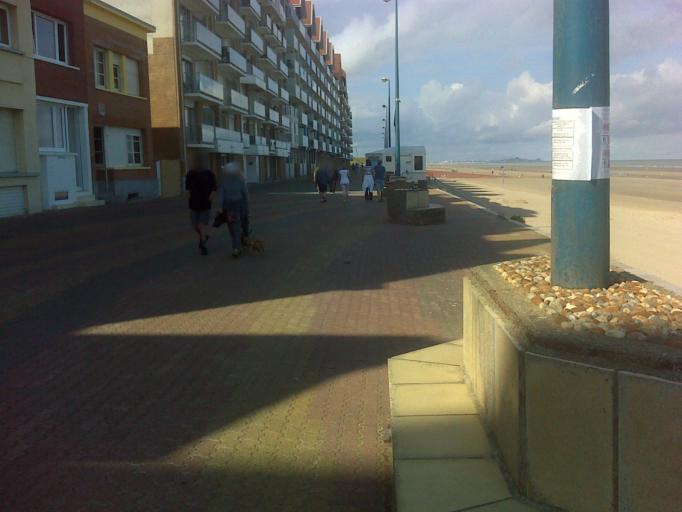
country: FR
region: Nord-Pas-de-Calais
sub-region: Departement du Nord
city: Bray-Dunes
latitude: 51.0784
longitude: 2.5104
